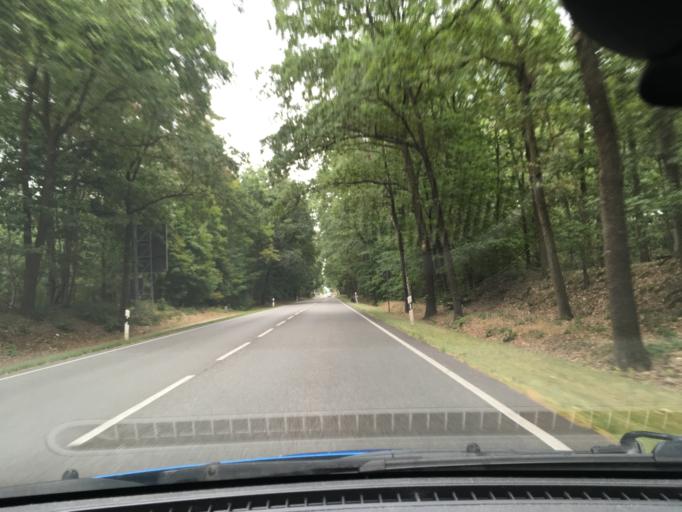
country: DE
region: Lower Saxony
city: Neu Wulmstorf
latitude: 53.4556
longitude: 9.7749
